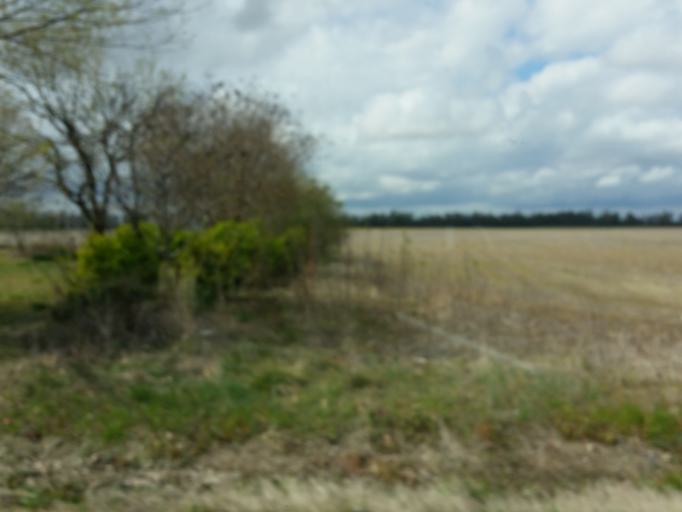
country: US
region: Arkansas
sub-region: Greene County
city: Marmaduke
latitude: 36.2358
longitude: -90.5353
